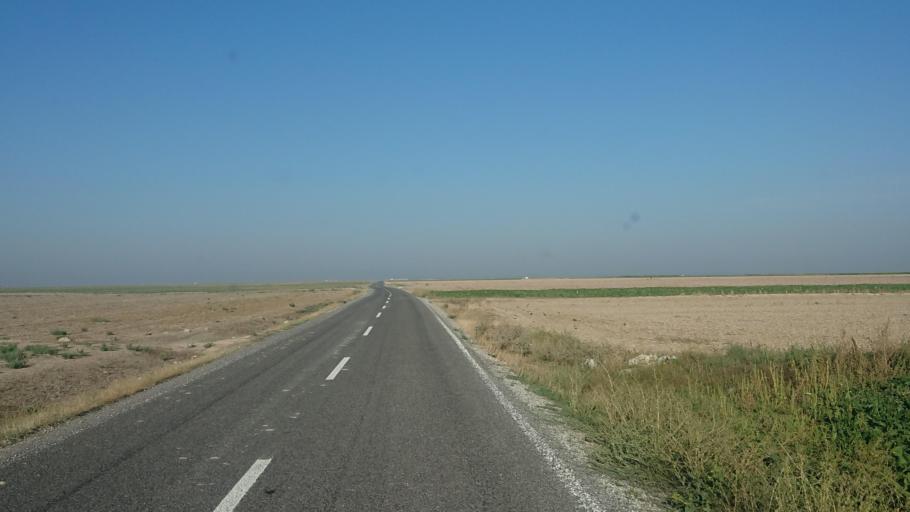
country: TR
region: Aksaray
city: Yesilova
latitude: 38.3877
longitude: 33.7885
